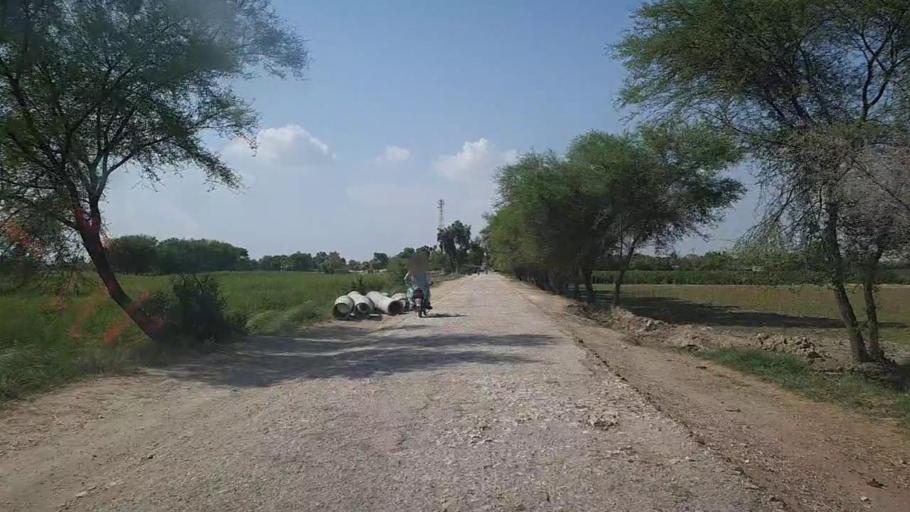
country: PK
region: Sindh
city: Khairpur
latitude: 28.1172
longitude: 69.6172
